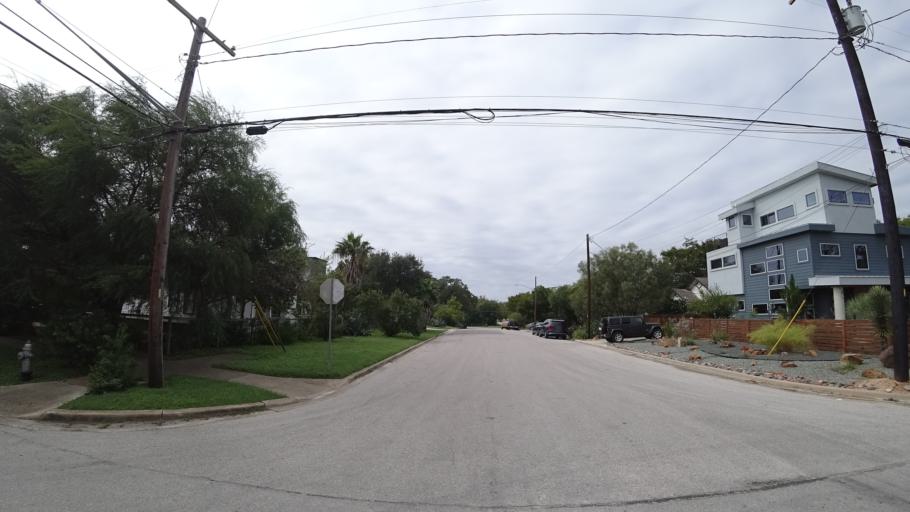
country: US
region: Texas
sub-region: Travis County
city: Austin
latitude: 30.2736
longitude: -97.7267
